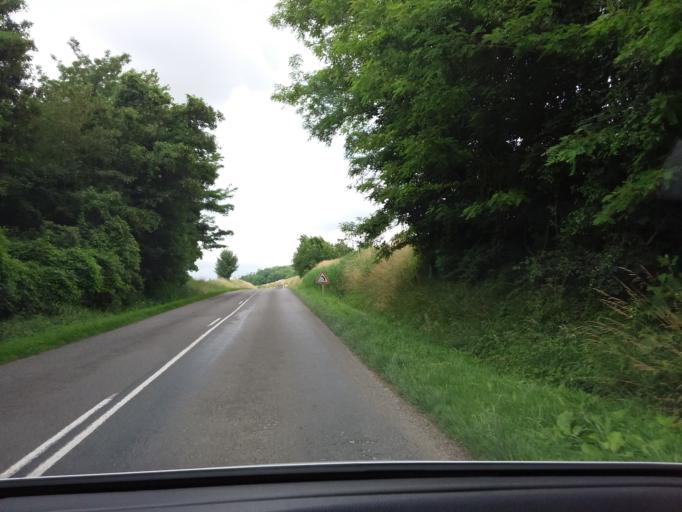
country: FR
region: Picardie
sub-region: Departement de l'Aisne
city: Bucy-le-Long
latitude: 49.3912
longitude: 3.4534
